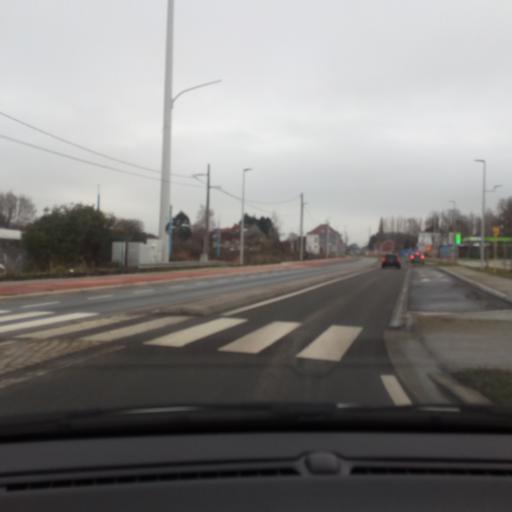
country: BE
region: Wallonia
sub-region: Province du Hainaut
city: Dour
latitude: 50.3977
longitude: 3.7675
